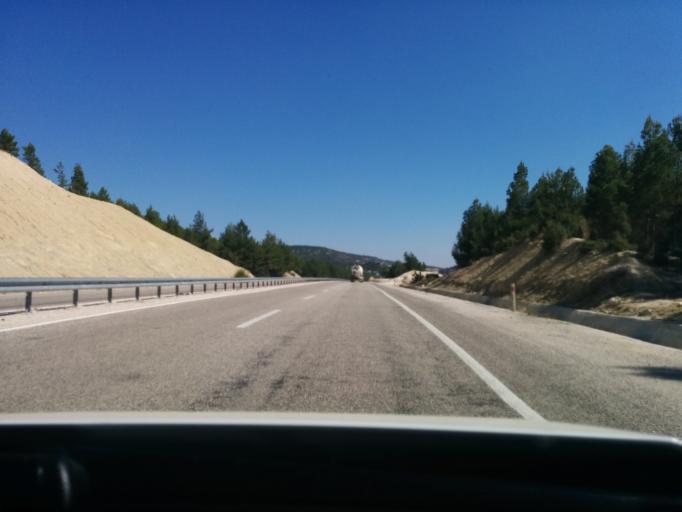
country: TR
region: Antalya
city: Korkuteli
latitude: 37.0486
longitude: 30.1409
